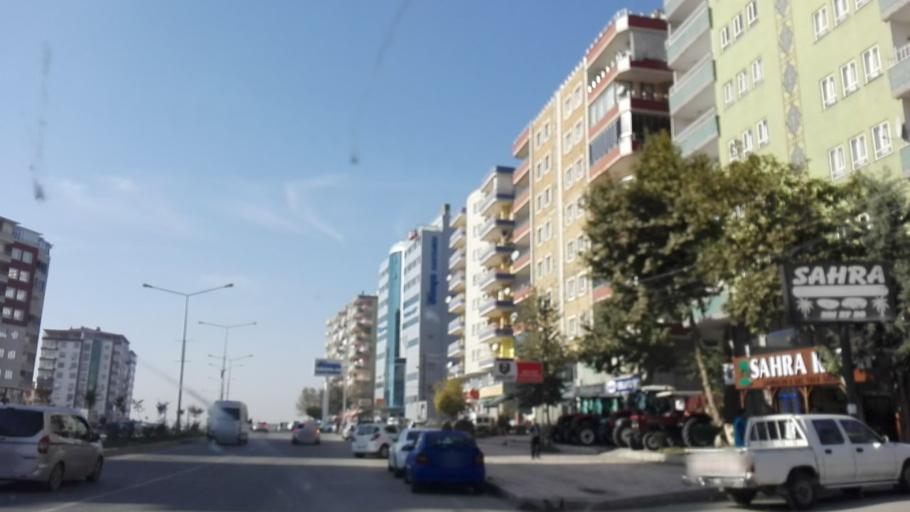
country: TR
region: Batman
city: Demiryol
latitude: 37.9016
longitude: 41.1442
